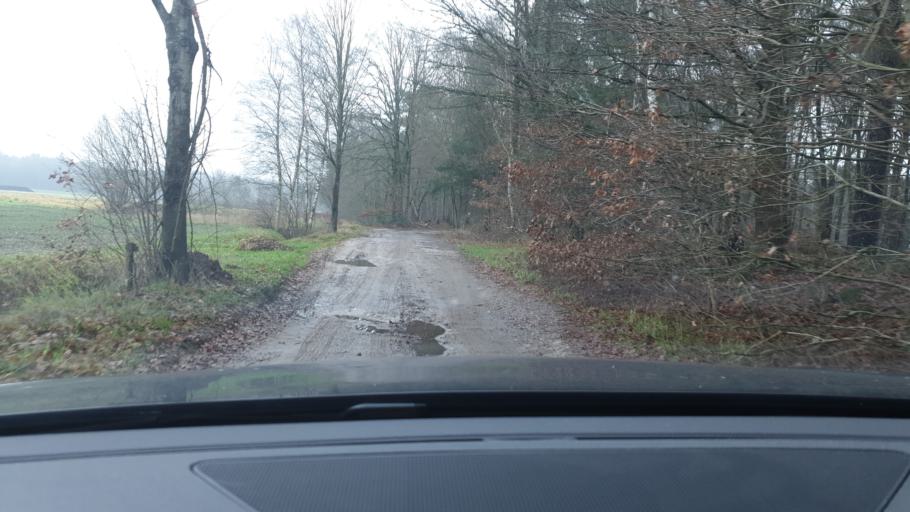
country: NL
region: North Brabant
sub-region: Gemeente Bladel en Netersel
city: Bladel
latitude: 51.3456
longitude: 5.1985
